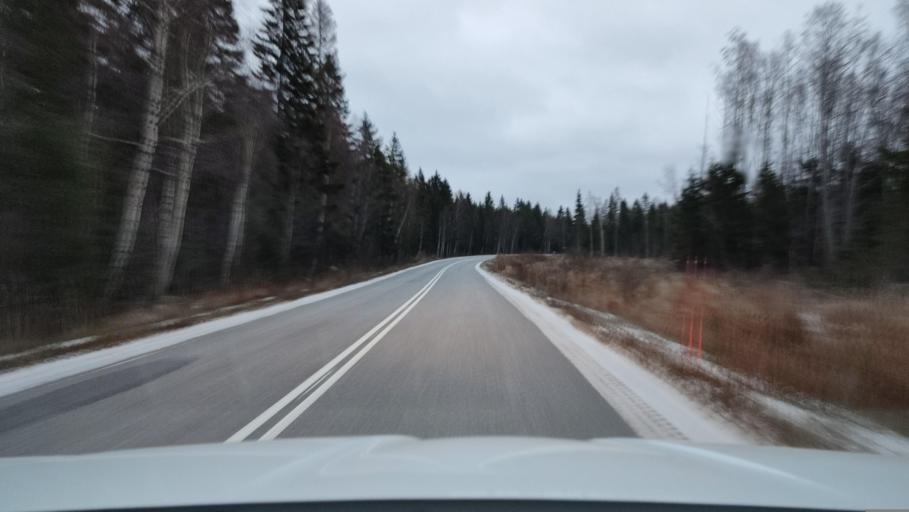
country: FI
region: Ostrobothnia
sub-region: Vaasa
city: Replot
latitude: 63.2657
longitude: 21.3526
